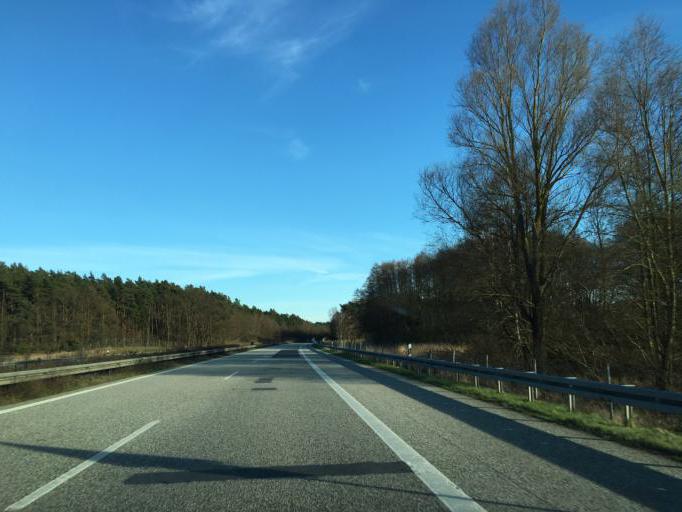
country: DE
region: Mecklenburg-Vorpommern
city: Malchow
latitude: 53.5079
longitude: 12.3709
